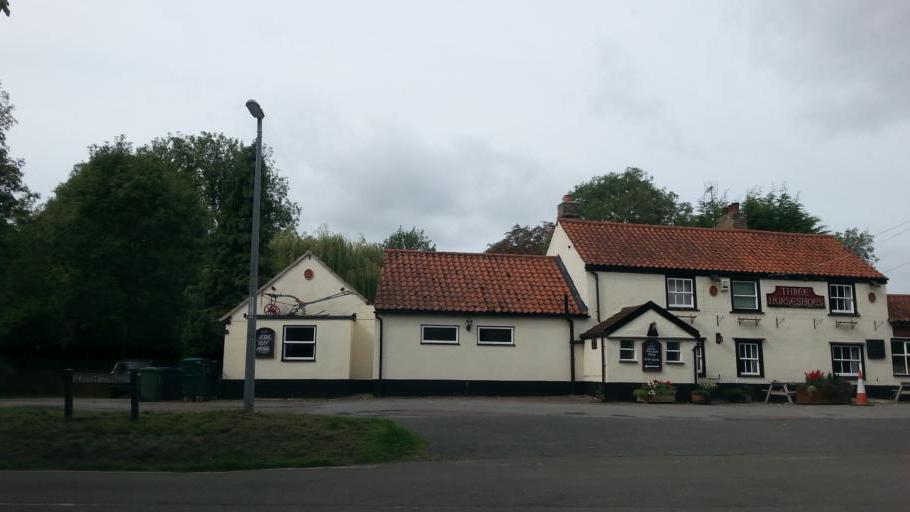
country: GB
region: England
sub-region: Cambridgeshire
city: Comberton
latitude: 52.1854
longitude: 0.0205
